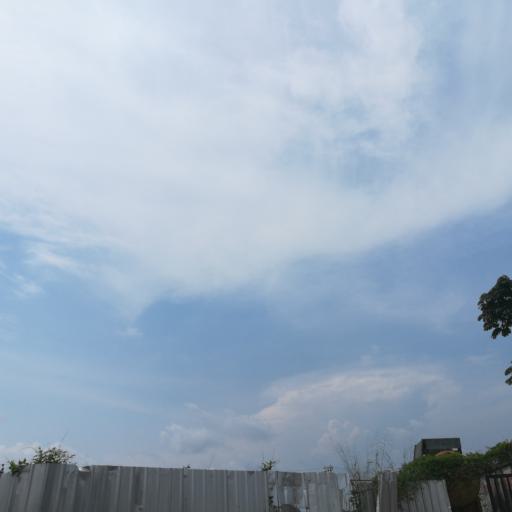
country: NG
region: Rivers
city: Port Harcourt
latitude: 4.8423
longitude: 7.0155
